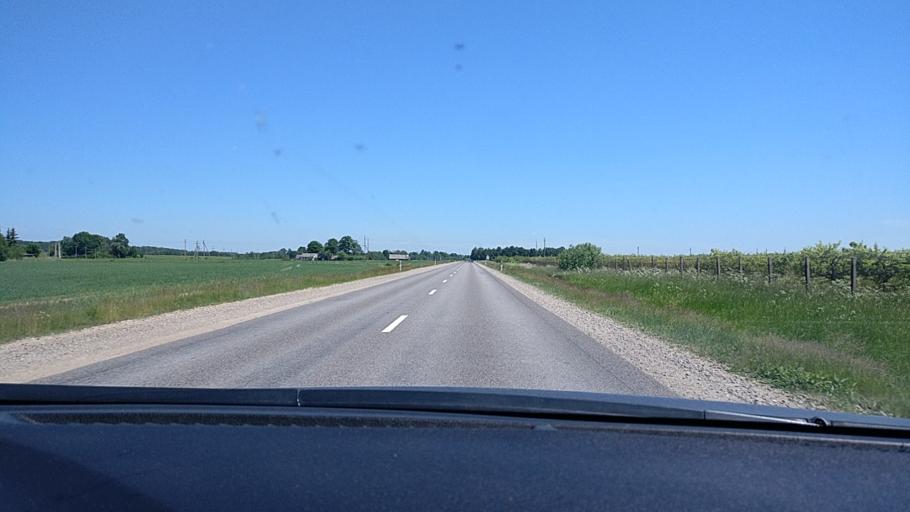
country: LT
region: Panevezys
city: Pasvalys
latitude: 56.1366
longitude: 24.5119
